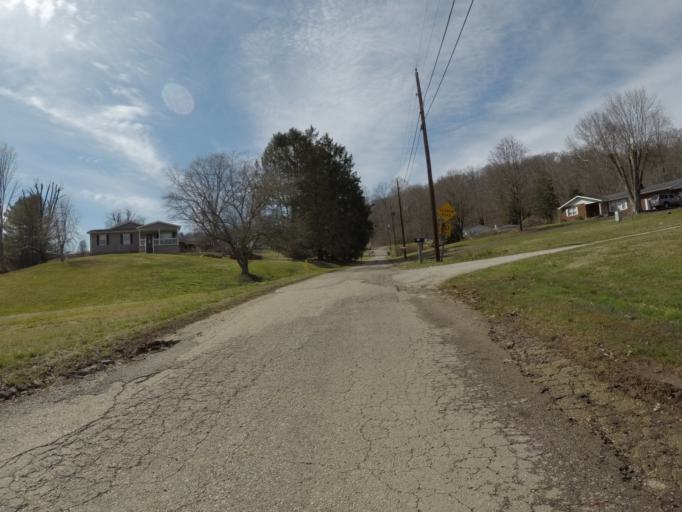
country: US
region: West Virginia
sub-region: Wayne County
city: Ceredo
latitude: 38.3611
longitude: -82.5350
